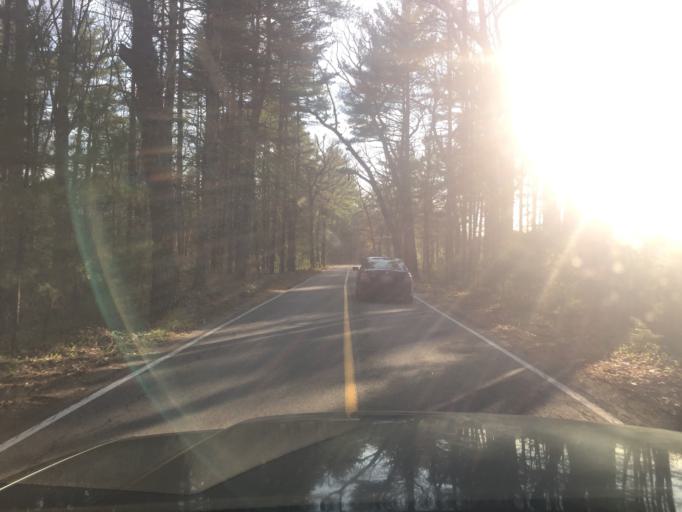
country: US
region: Massachusetts
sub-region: Middlesex County
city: Sherborn
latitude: 42.2280
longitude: -71.3465
